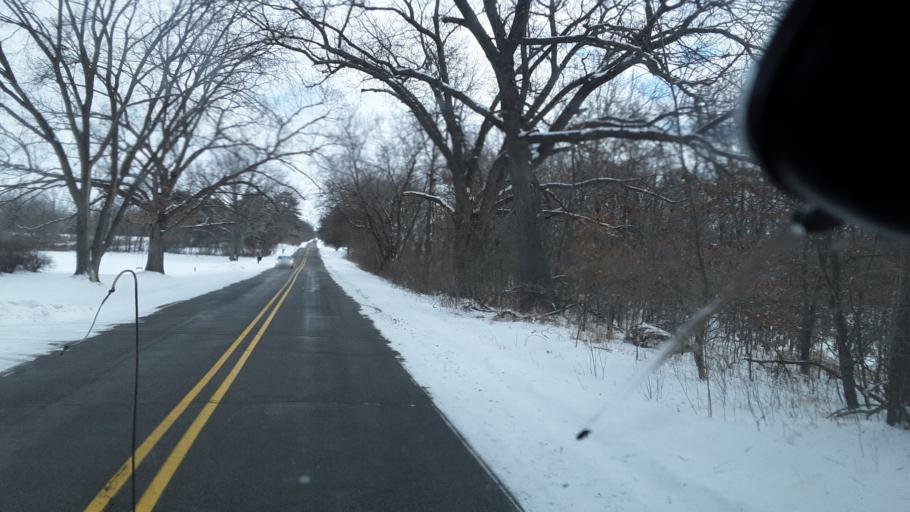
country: US
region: Michigan
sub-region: Ingham County
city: Leslie
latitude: 42.4715
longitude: -84.3532
